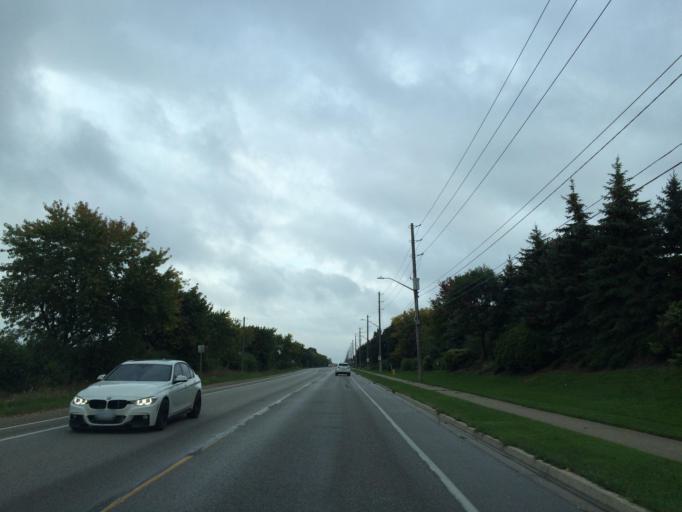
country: CA
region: Ontario
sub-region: Wellington County
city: Guelph
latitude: 43.5213
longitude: -80.1819
